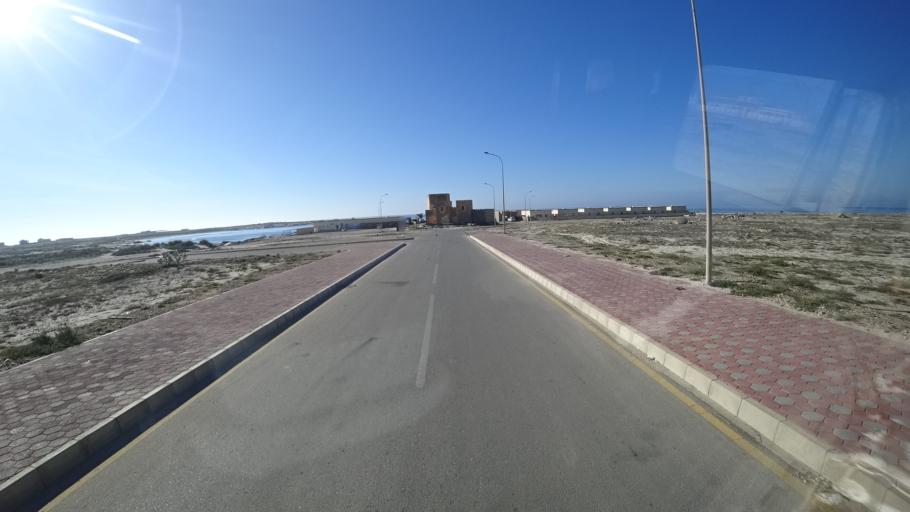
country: OM
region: Zufar
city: Salalah
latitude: 16.9774
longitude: 54.6919
